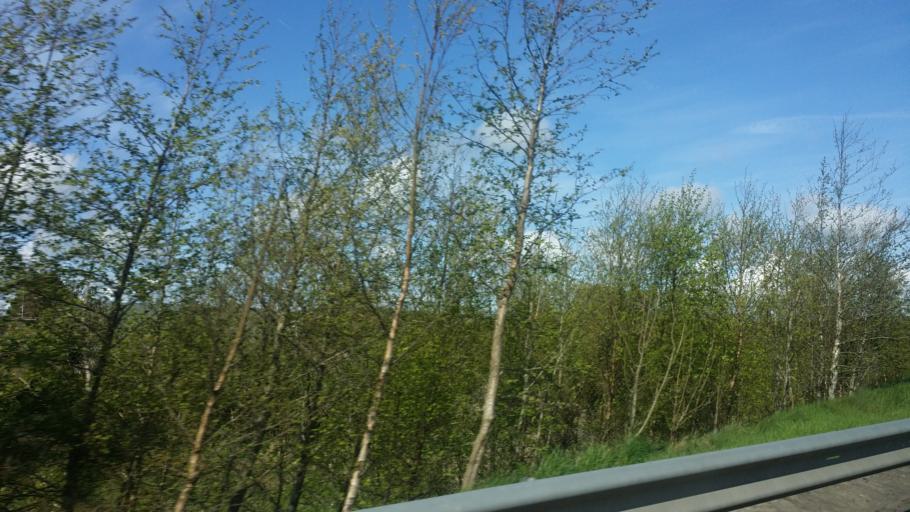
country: IE
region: Ulster
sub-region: An Cabhan
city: Mullagh
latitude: 53.7373
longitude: -6.9661
